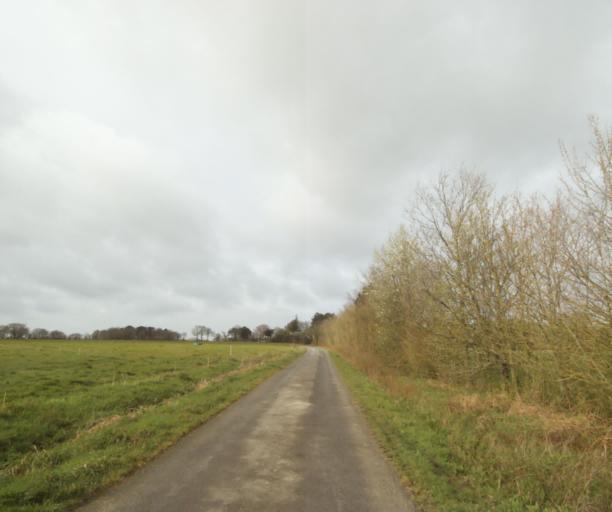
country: FR
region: Pays de la Loire
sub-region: Departement de la Loire-Atlantique
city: Bouvron
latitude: 47.3990
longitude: -1.8774
